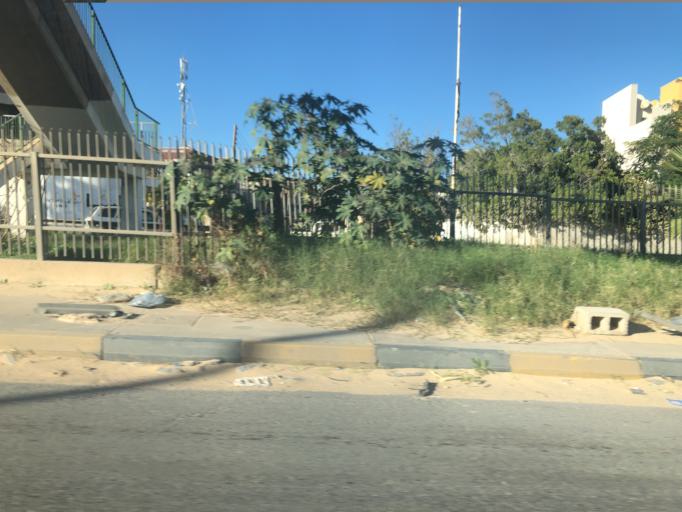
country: LY
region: Tripoli
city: Tripoli
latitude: 32.8698
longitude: 13.2623
